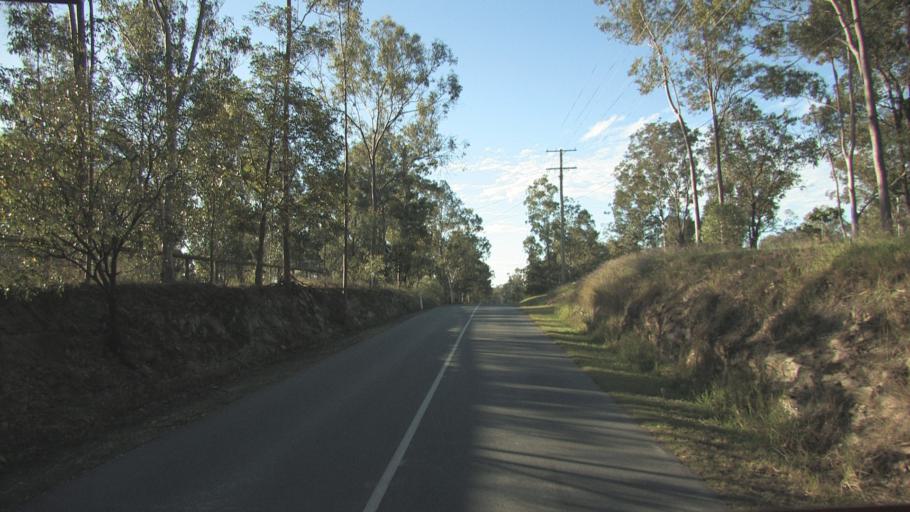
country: AU
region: Queensland
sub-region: Logan
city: Waterford West
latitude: -27.7256
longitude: 153.1473
